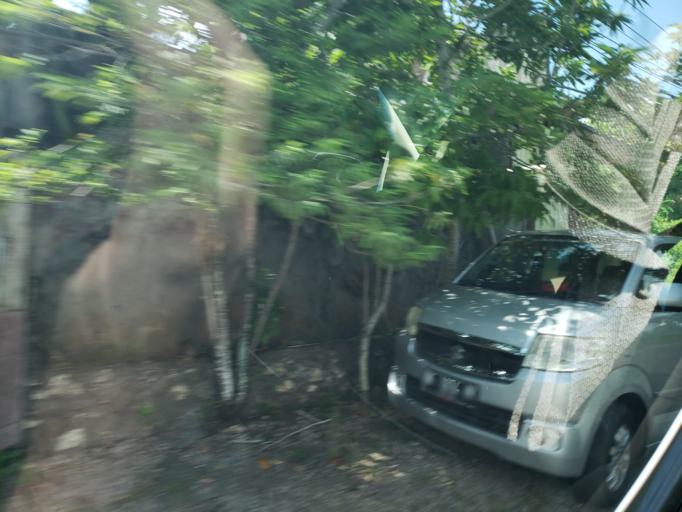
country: ID
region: Bali
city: Kangin
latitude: -8.8217
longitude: 115.1526
